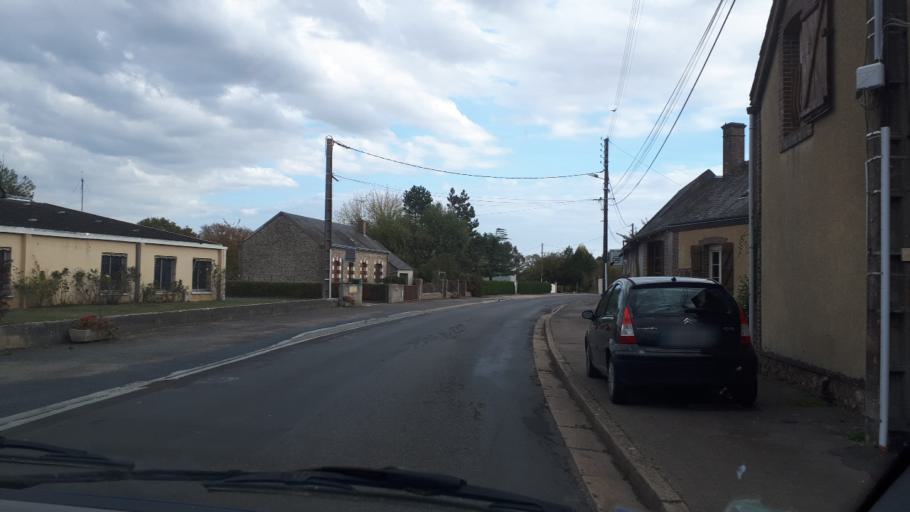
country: FR
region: Centre
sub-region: Departement du Loir-et-Cher
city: Mondoubleau
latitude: 48.0365
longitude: 0.9277
